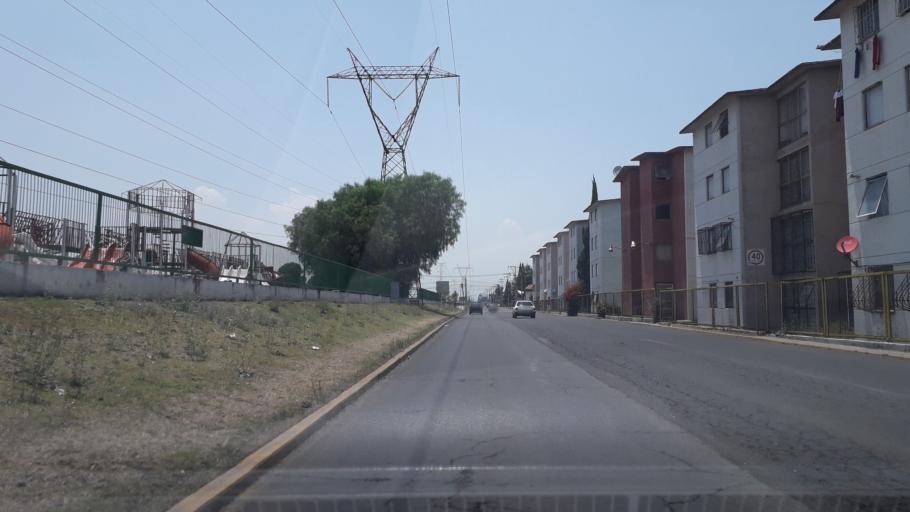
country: MX
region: Mexico
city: Santiago Teyahualco
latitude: 19.6419
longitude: -99.1192
